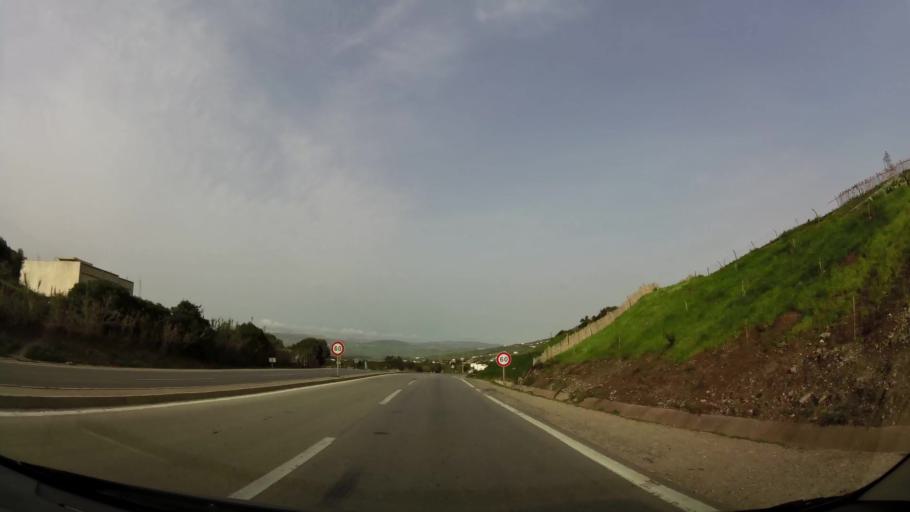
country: MA
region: Tanger-Tetouan
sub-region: Tetouan
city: Saddina
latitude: 35.5491
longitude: -5.5252
